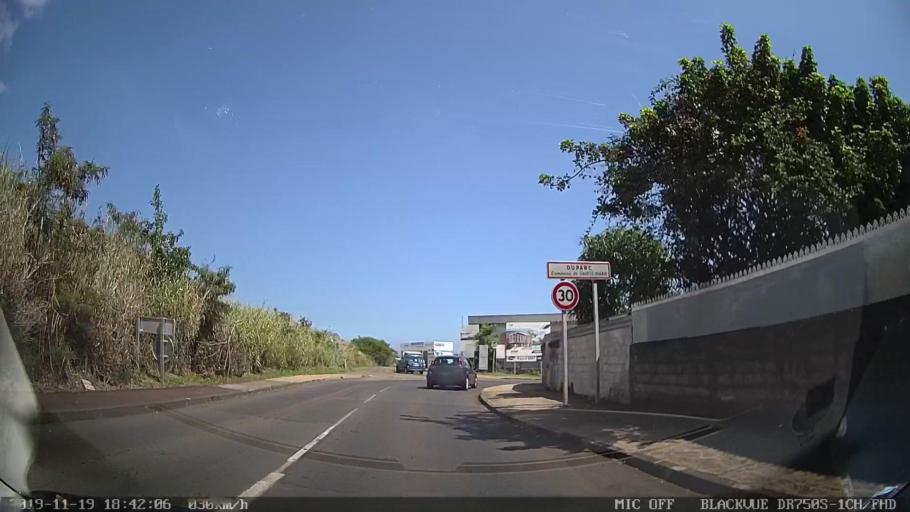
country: RE
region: Reunion
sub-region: Reunion
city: Sainte-Marie
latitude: -20.9143
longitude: 55.5180
